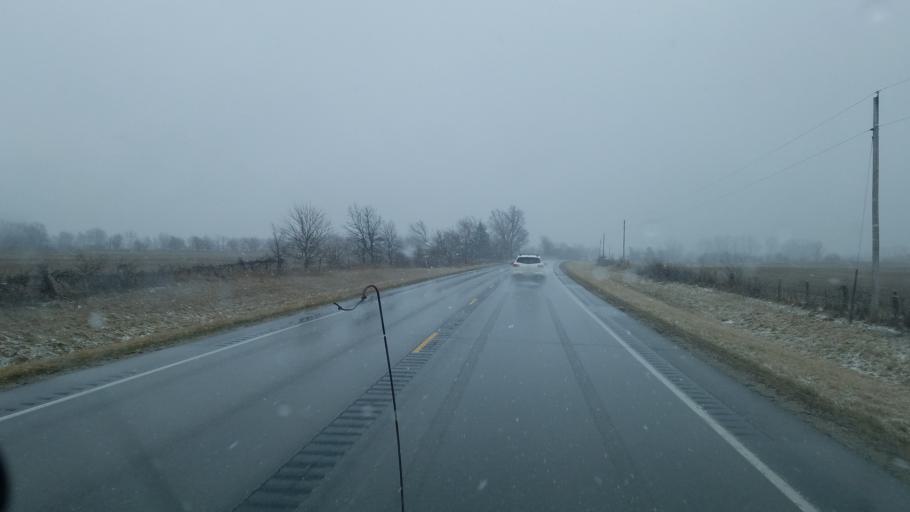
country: US
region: Indiana
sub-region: Grant County
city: Sweetser
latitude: 40.6498
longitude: -85.7102
